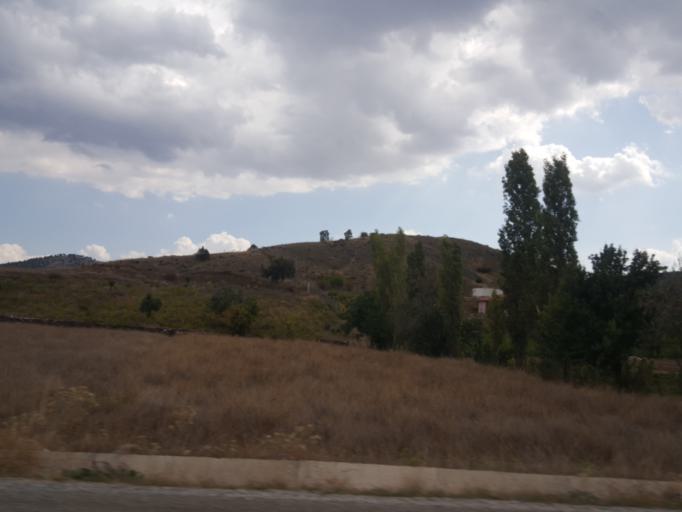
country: TR
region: Yozgat
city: Cekerek
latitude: 40.1944
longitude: 35.4499
